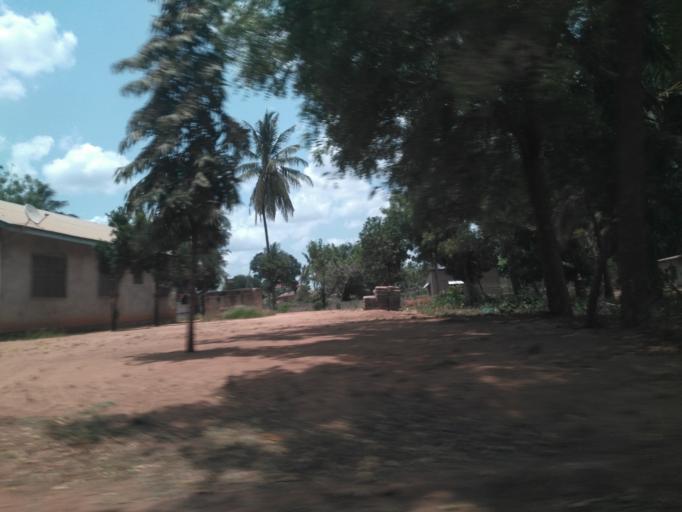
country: TZ
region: Dar es Salaam
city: Dar es Salaam
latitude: -6.8408
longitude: 39.3369
